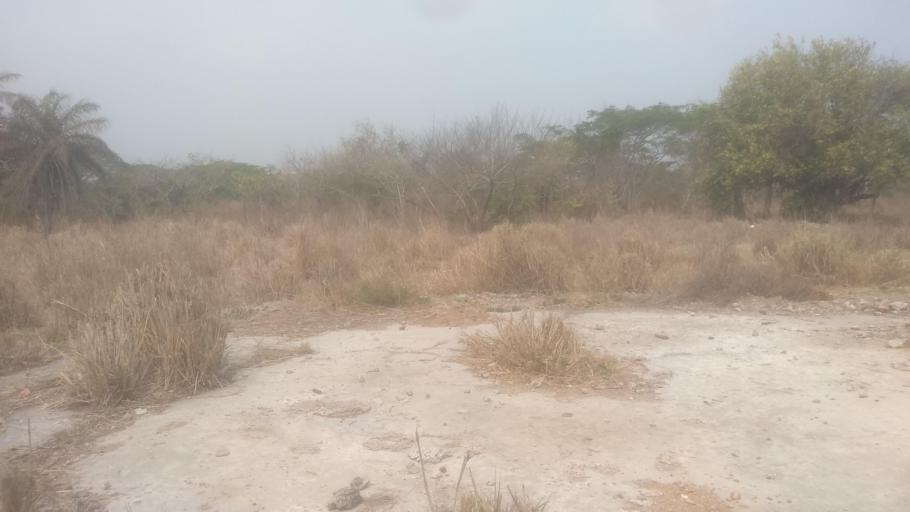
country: MX
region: Veracruz
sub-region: Veracruz
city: Oasis
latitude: 19.1922
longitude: -96.2239
